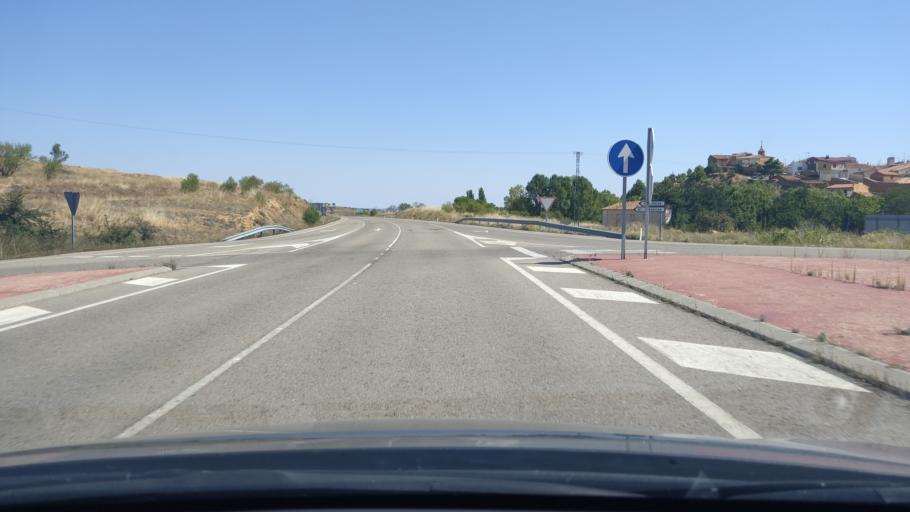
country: ES
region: Aragon
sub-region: Provincia de Teruel
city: Cortes de Aragon
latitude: 40.9721
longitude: -0.8395
